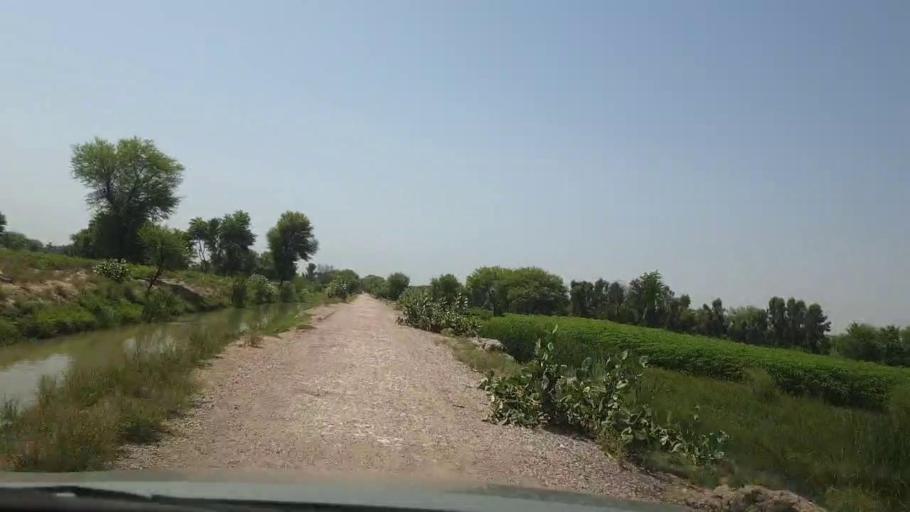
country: PK
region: Sindh
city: Rohri
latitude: 27.6576
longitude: 68.9822
